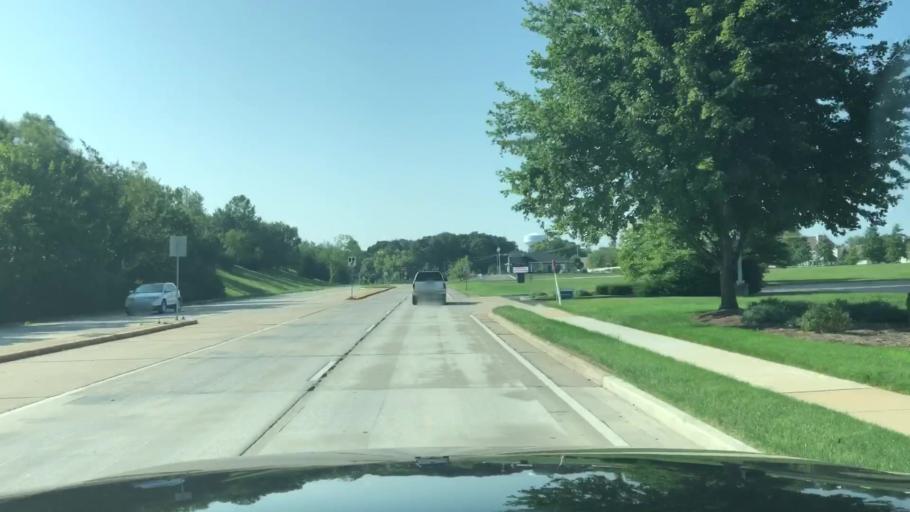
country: US
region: Missouri
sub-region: Saint Charles County
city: Saint Charles
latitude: 38.7746
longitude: -90.5272
